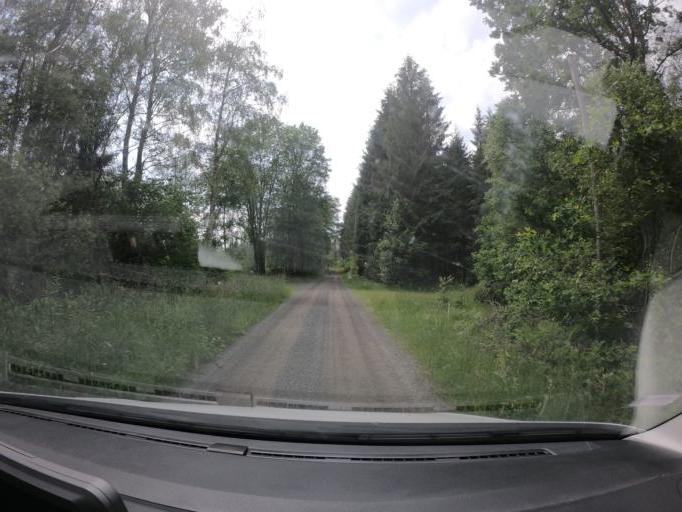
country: SE
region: Skane
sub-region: Hassleholms Kommun
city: Bjarnum
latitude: 56.2131
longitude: 13.5494
